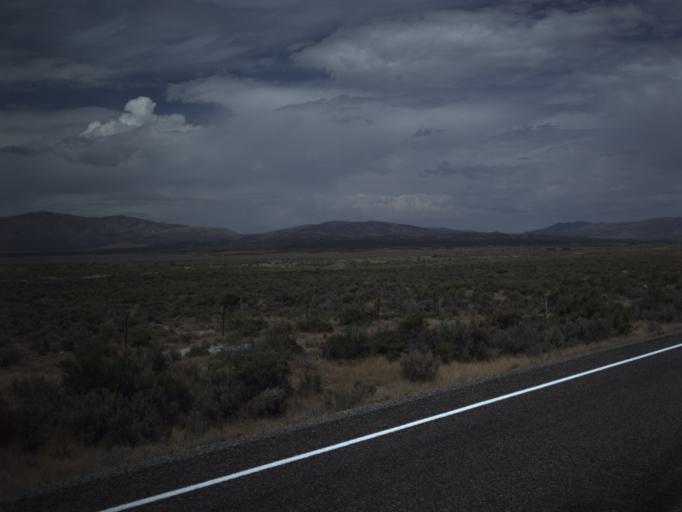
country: US
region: Idaho
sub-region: Cassia County
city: Burley
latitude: 41.6609
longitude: -113.5477
